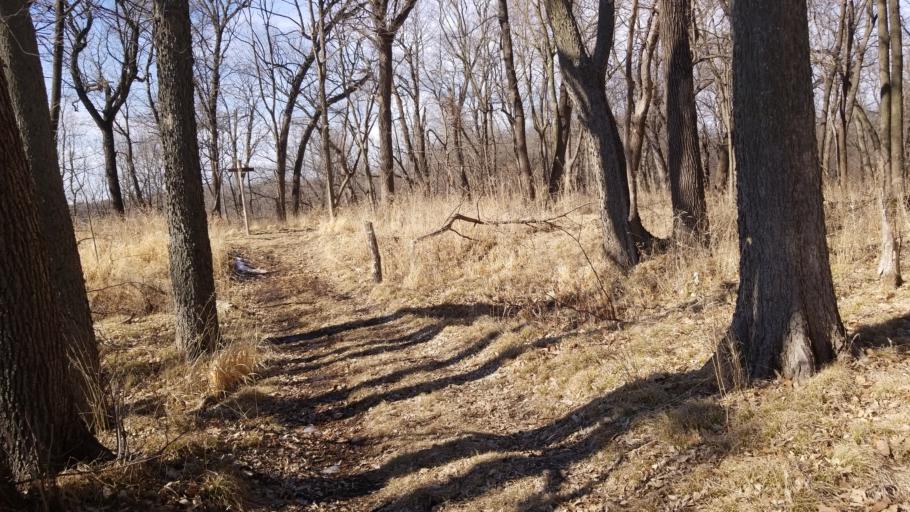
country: US
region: Nebraska
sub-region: Sarpy County
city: Bellevue
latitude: 41.1703
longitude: -95.9021
